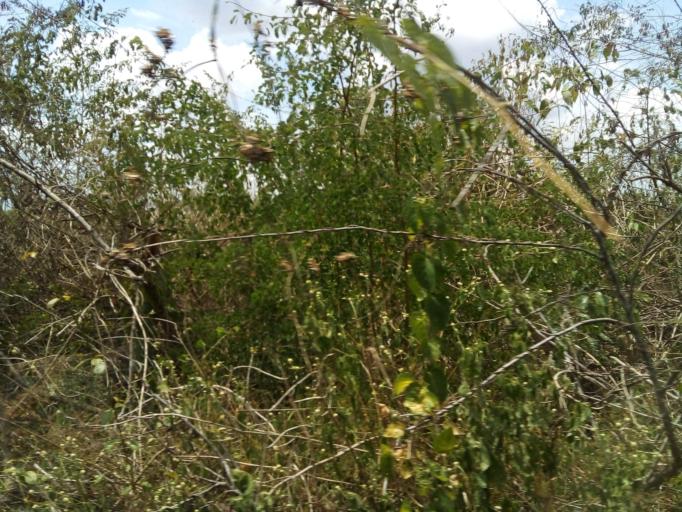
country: BR
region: Maranhao
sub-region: Itapecuru Mirim
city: Itapecuru Mirim
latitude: -3.1347
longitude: -44.3364
